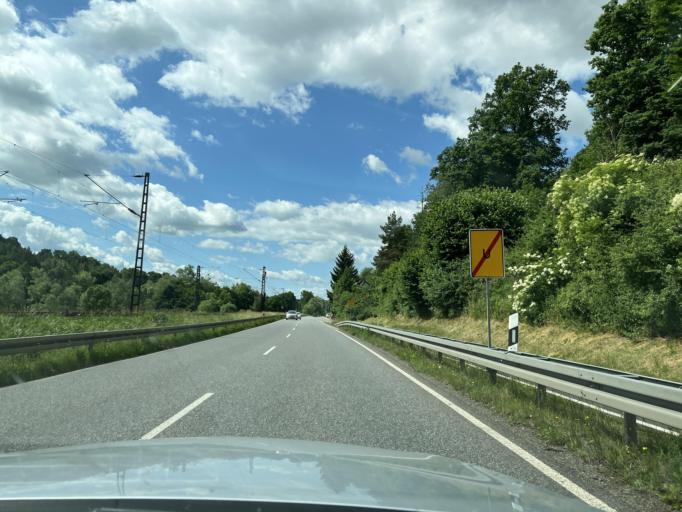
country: DE
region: Hesse
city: Neustadt (Hessen)
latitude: 50.8888
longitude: 9.1429
